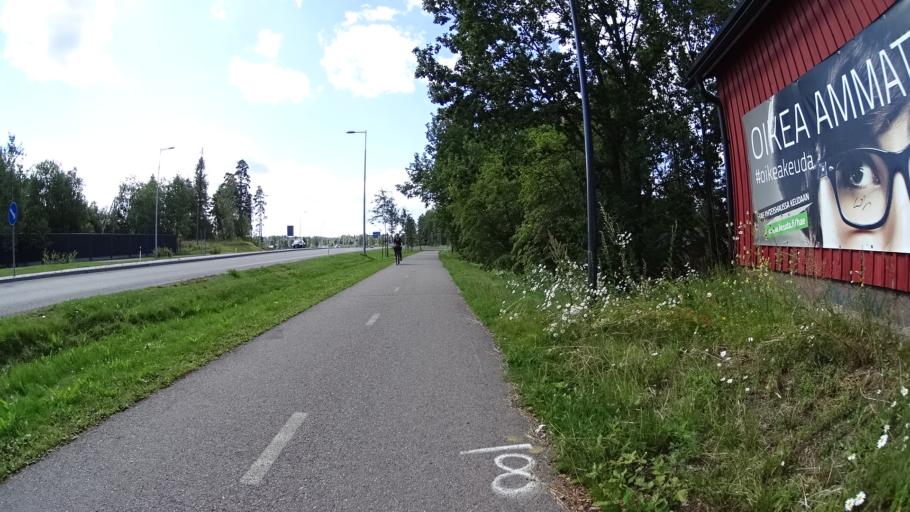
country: FI
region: Uusimaa
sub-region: Helsinki
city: Jaervenpaeae
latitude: 60.4574
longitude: 25.0838
